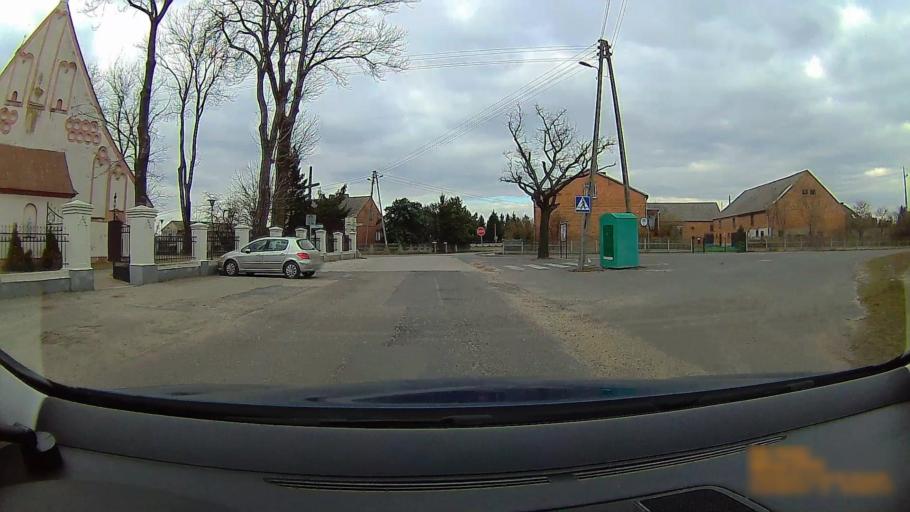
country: PL
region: Greater Poland Voivodeship
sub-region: Powiat koninski
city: Rzgow Pierwszy
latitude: 52.1337
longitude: 18.0574
